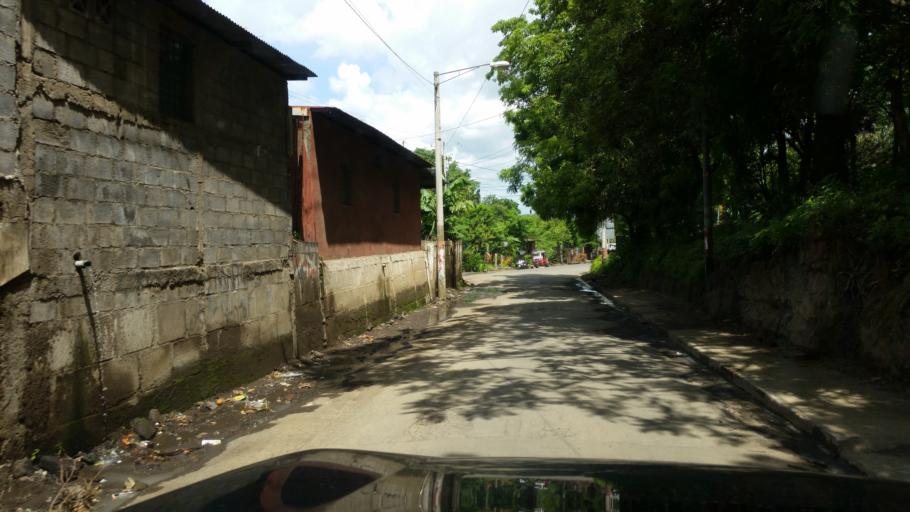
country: NI
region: Masaya
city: Ticuantepe
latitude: 12.0762
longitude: -86.2162
